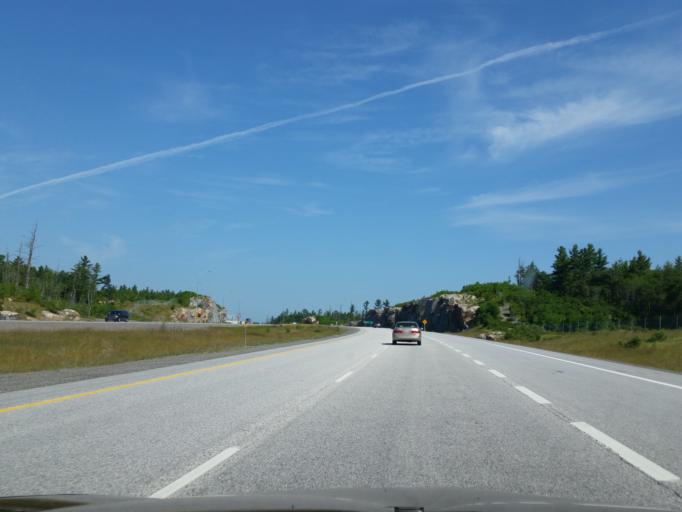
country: CA
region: Ontario
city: Greater Sudbury
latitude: 46.2299
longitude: -80.7731
